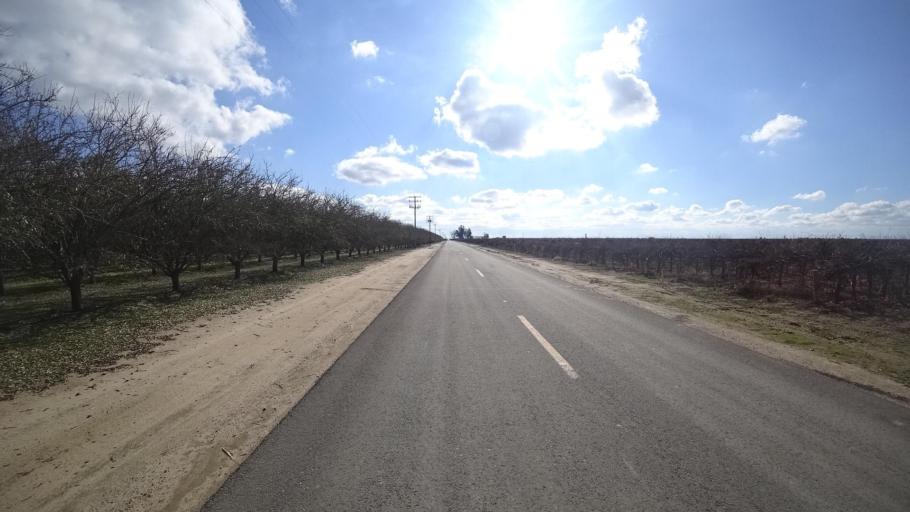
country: US
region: California
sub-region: Kern County
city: Delano
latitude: 35.7514
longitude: -119.3657
